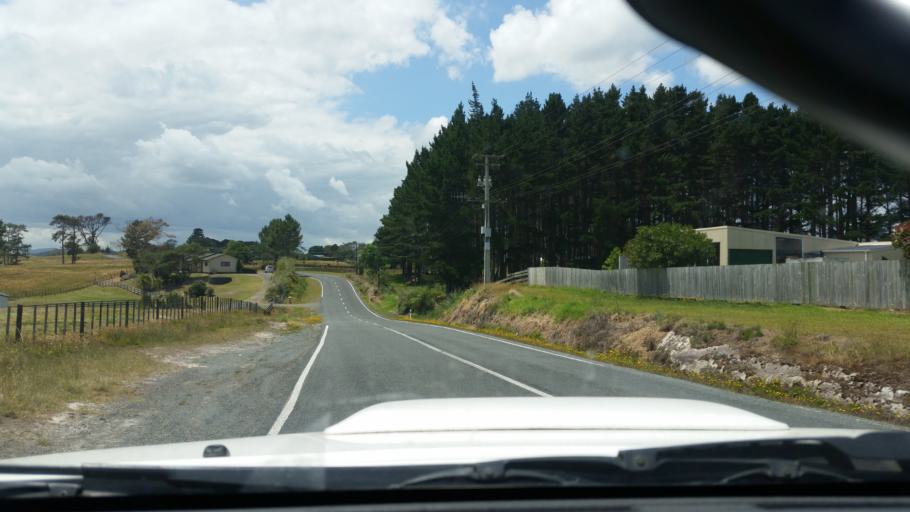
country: NZ
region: Northland
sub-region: Kaipara District
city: Dargaville
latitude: -35.9185
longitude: 173.8194
